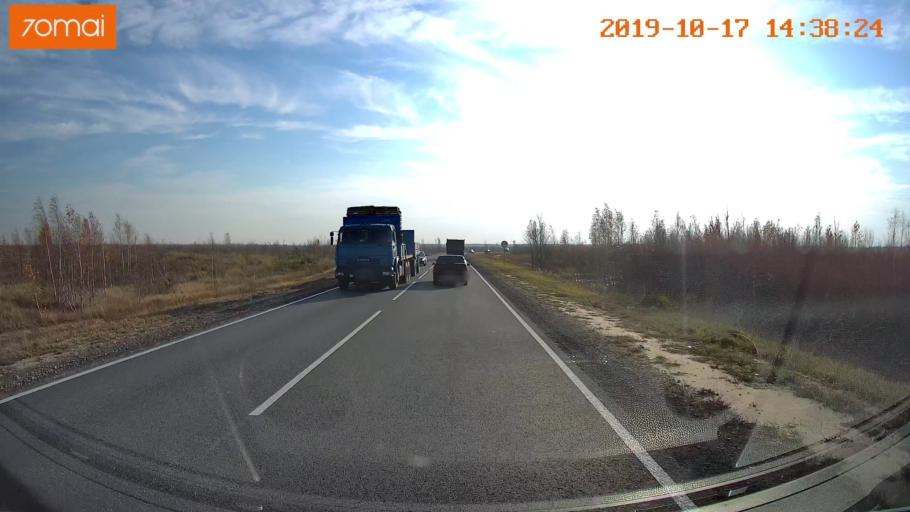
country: RU
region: Rjazan
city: Solotcha
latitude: 54.8706
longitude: 39.9847
